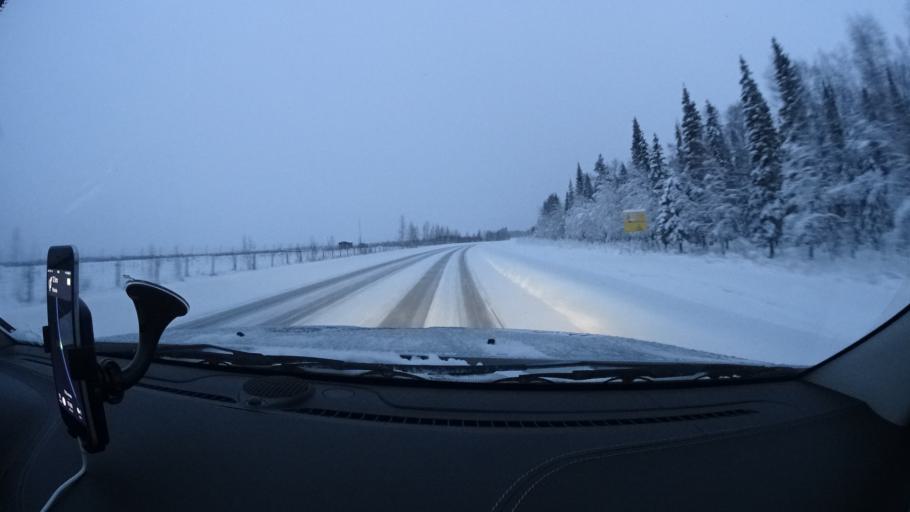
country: FI
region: Lapland
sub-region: Tunturi-Lappi
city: Kittilae
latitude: 67.7061
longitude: 24.8500
